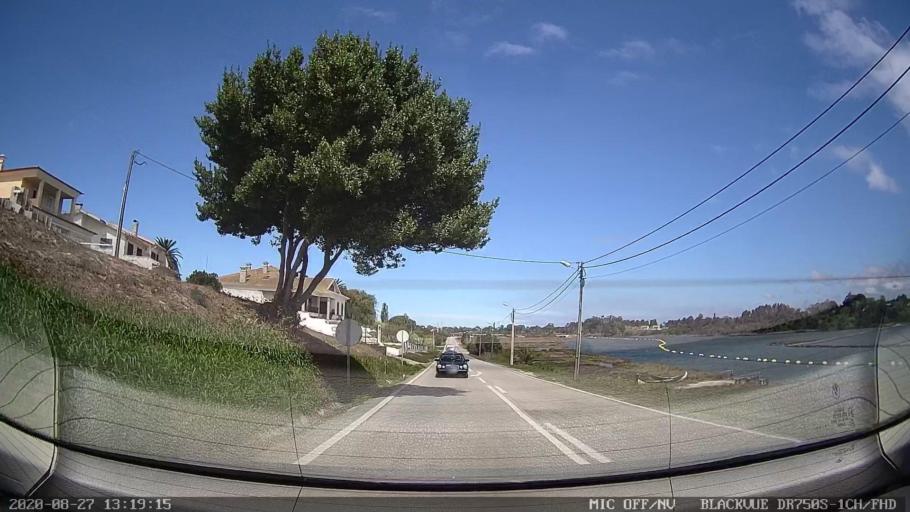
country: PT
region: Aveiro
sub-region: Vagos
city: Vagos
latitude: 40.5658
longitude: -8.6825
